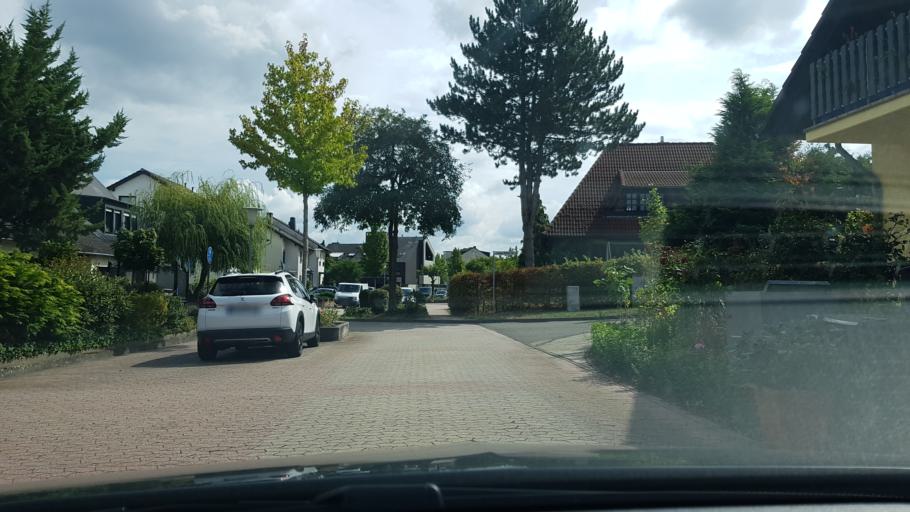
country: DE
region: Rheinland-Pfalz
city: Andernach
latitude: 50.4202
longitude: 7.4022
